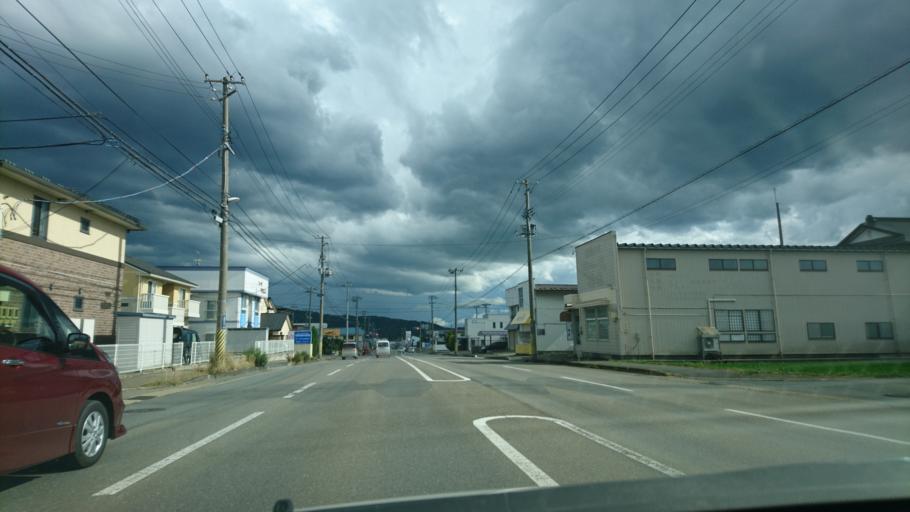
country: JP
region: Iwate
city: Kitakami
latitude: 39.3015
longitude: 141.1285
